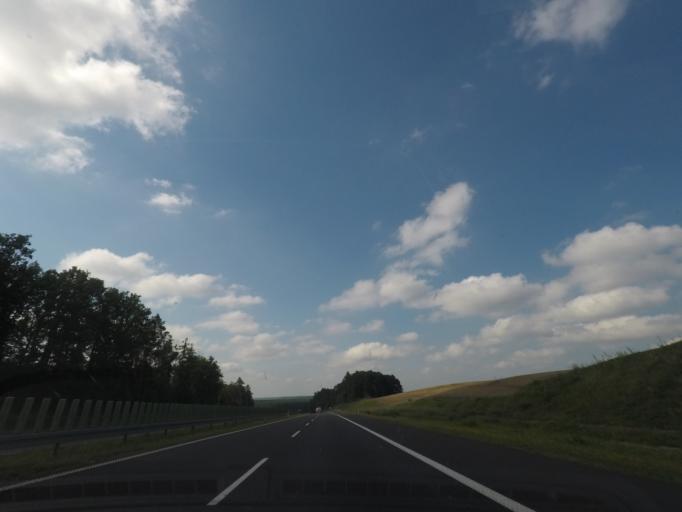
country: PL
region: Kujawsko-Pomorskie
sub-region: Powiat swiecki
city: Warlubie
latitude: 53.5336
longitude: 18.6023
